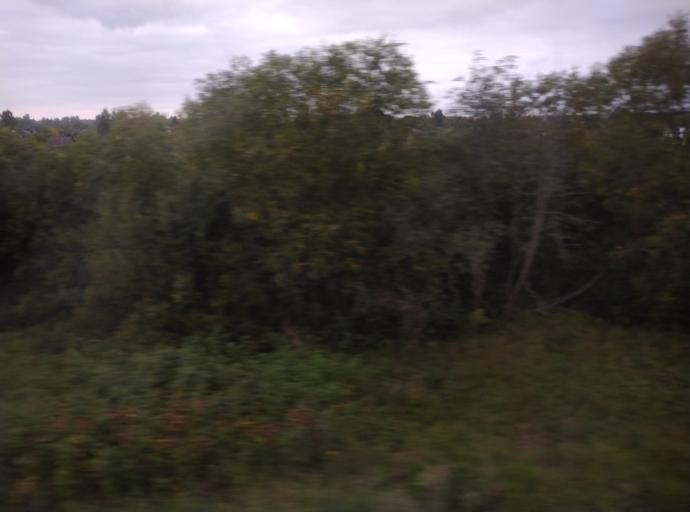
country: RU
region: Kostroma
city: Nerekhta
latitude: 57.4739
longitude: 40.5770
